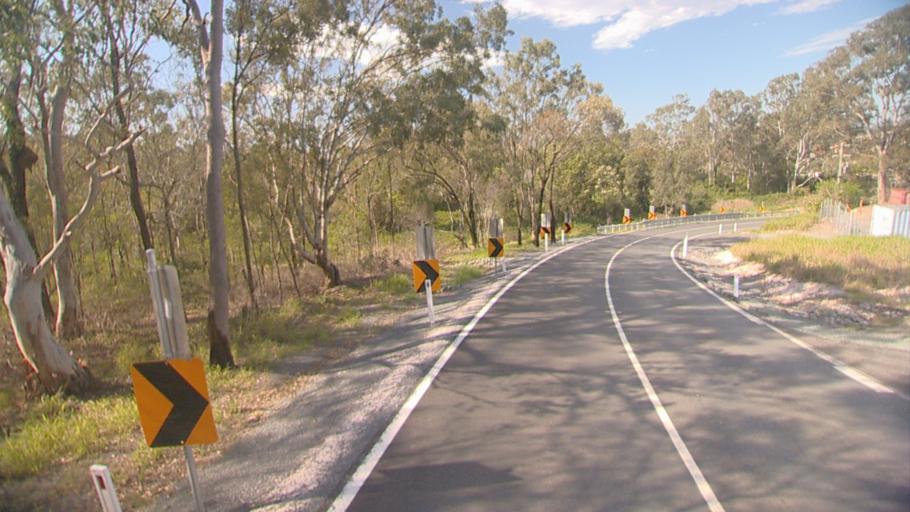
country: AU
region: Queensland
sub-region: Logan
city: Windaroo
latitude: -27.7281
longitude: 153.1908
